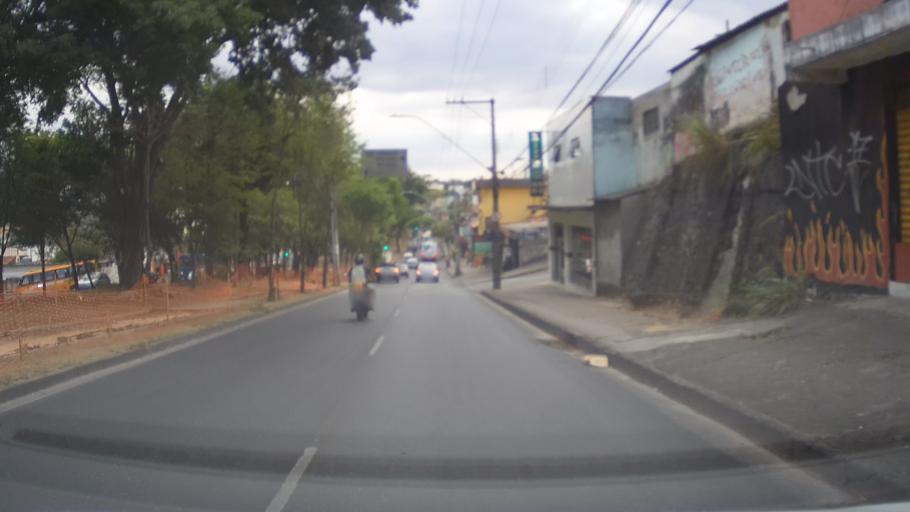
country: BR
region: Minas Gerais
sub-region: Belo Horizonte
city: Belo Horizonte
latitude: -19.8773
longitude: -43.9110
